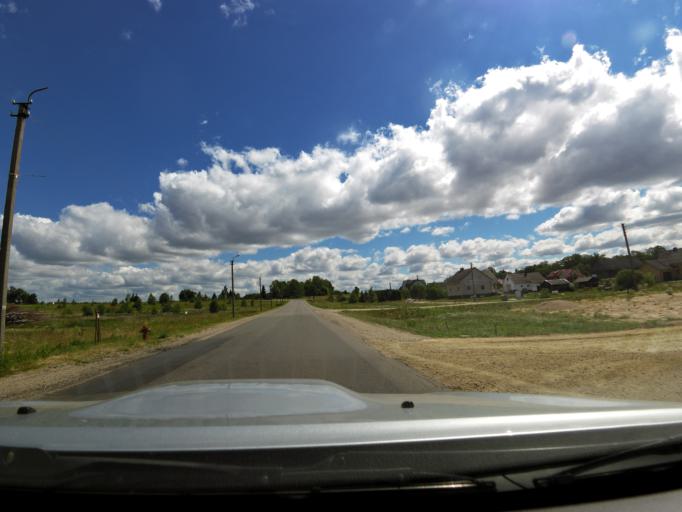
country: LT
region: Panevezys
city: Rokiskis
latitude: 55.9689
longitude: 25.5945
